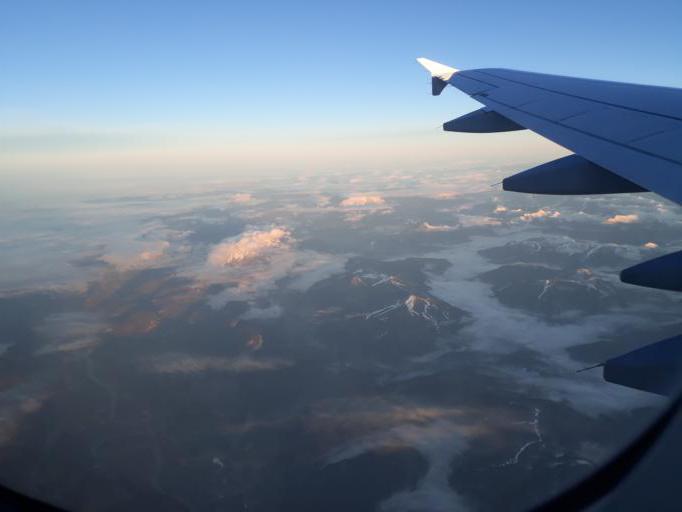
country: AT
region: Tyrol
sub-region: Politischer Bezirk Kufstein
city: Radfeld
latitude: 47.4433
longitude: 11.9392
